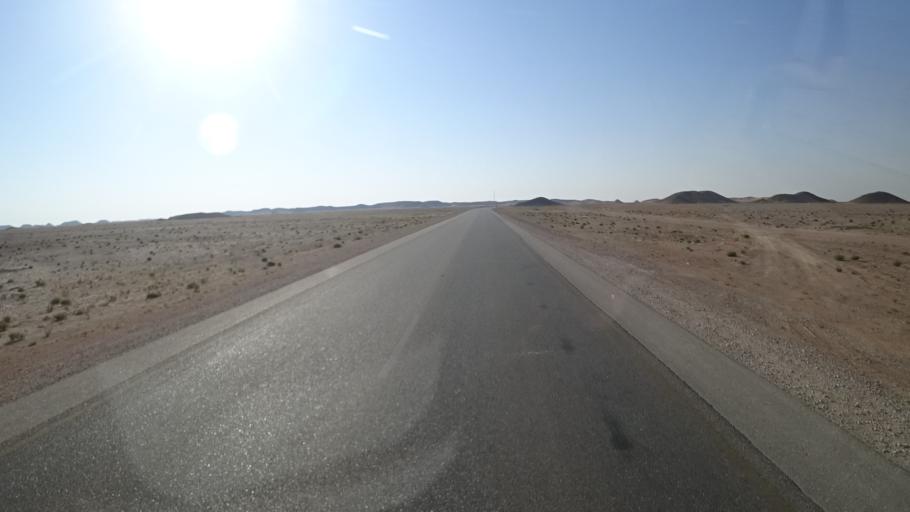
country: OM
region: Zufar
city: Salalah
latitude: 17.6392
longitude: 53.8776
